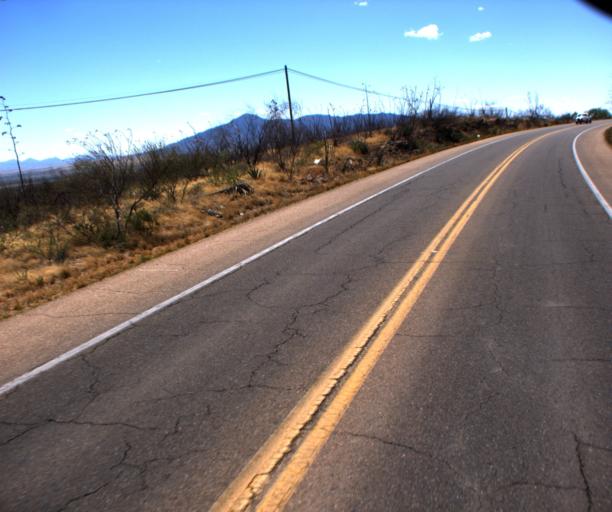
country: US
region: Arizona
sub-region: Cochise County
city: Bisbee
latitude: 31.4063
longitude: -109.9045
